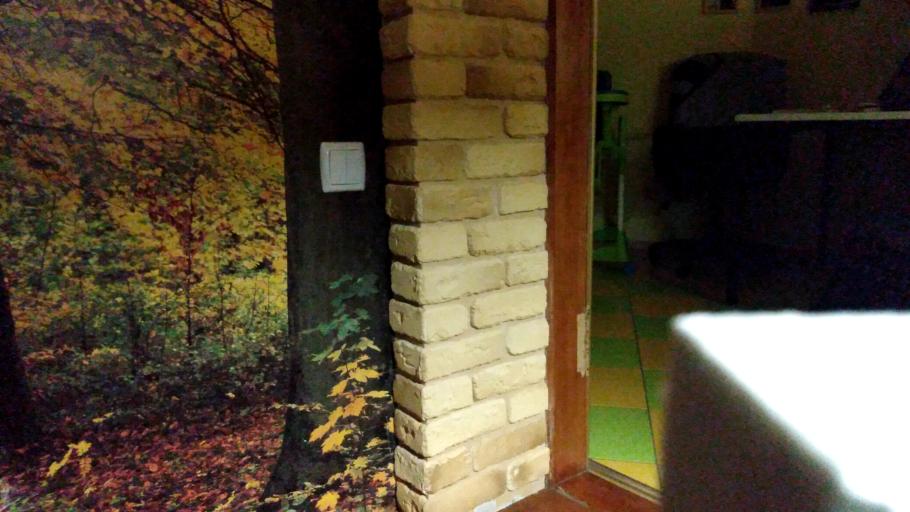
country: RU
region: Vologda
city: Lipin Bor
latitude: 61.0595
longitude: 37.9394
